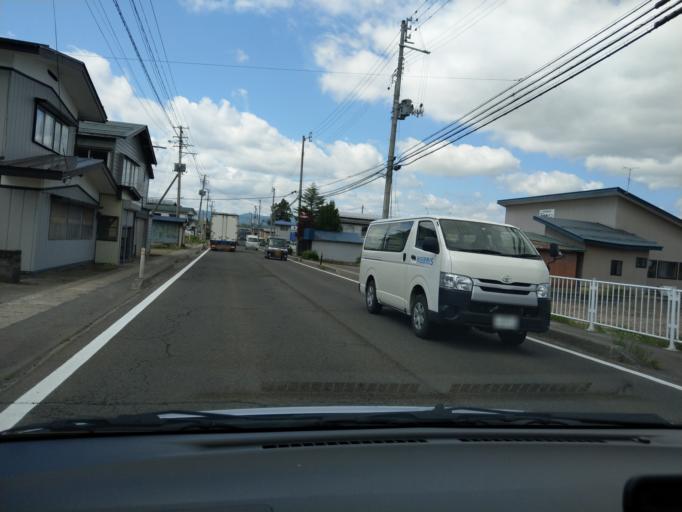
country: JP
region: Akita
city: Yuzawa
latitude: 39.1876
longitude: 140.5007
